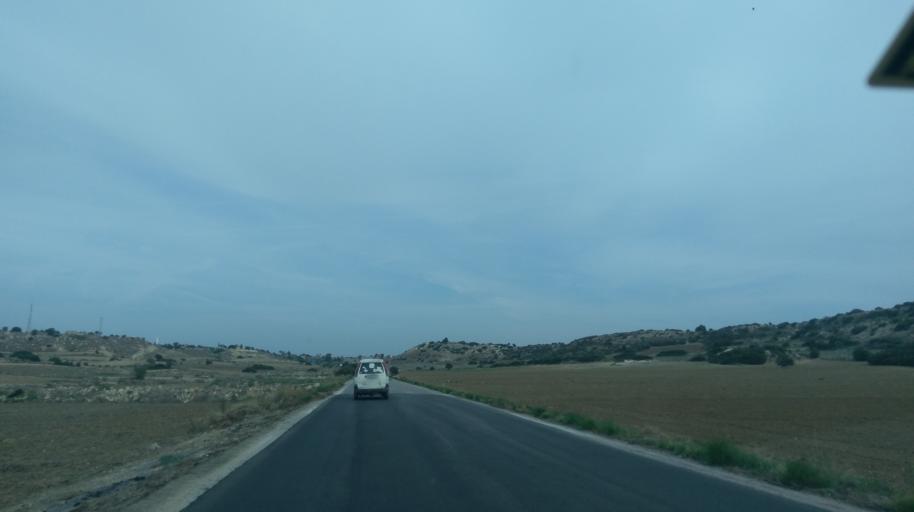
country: CY
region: Ammochostos
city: Leonarisso
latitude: 35.4600
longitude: 34.1329
